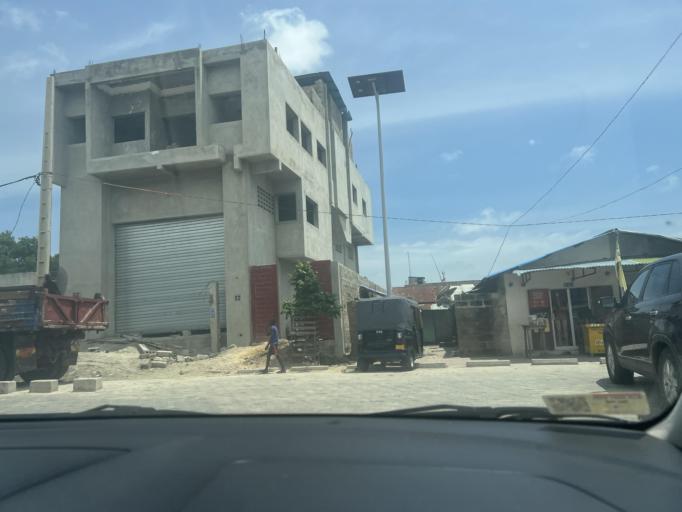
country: BJ
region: Littoral
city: Cotonou
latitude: 6.3886
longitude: 2.4377
